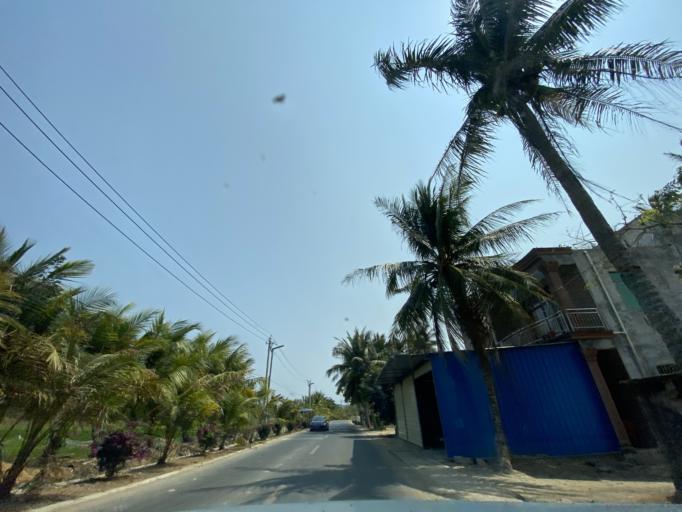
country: CN
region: Hainan
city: Yingzhou
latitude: 18.4142
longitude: 109.8149
